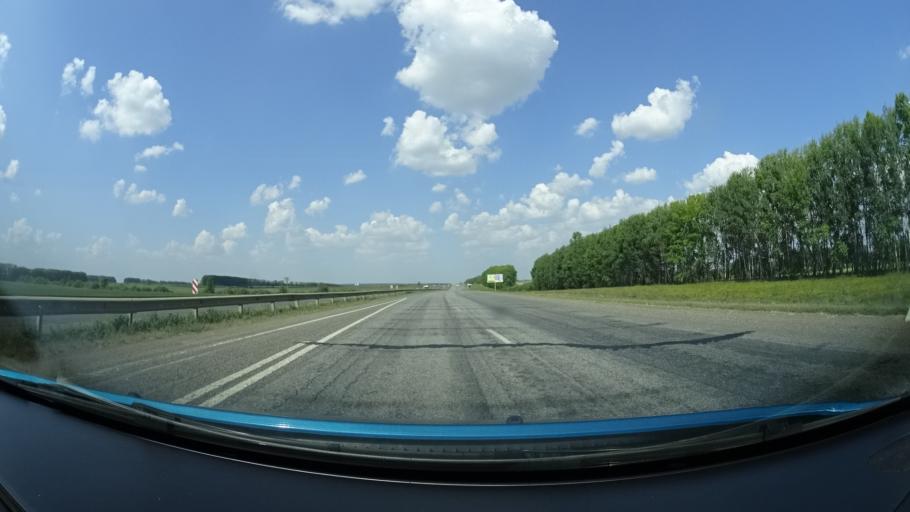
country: RU
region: Bashkortostan
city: Alekseyevka
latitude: 54.7196
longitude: 55.1826
